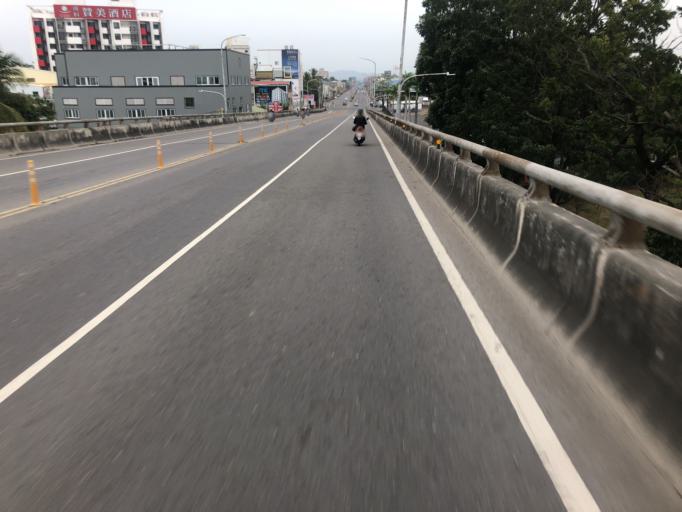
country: TW
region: Taiwan
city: Yujing
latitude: 23.1305
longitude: 120.3062
